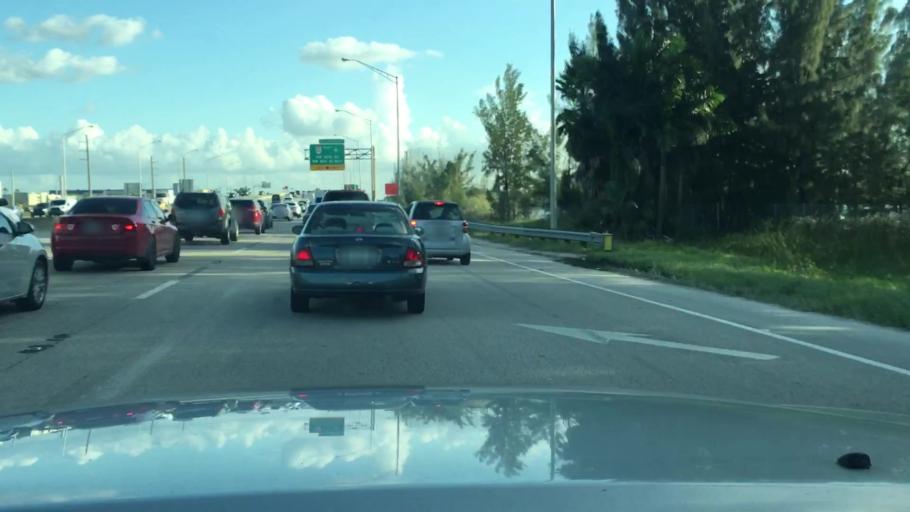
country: US
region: Florida
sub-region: Miami-Dade County
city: Doral
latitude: 25.8012
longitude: -80.3863
